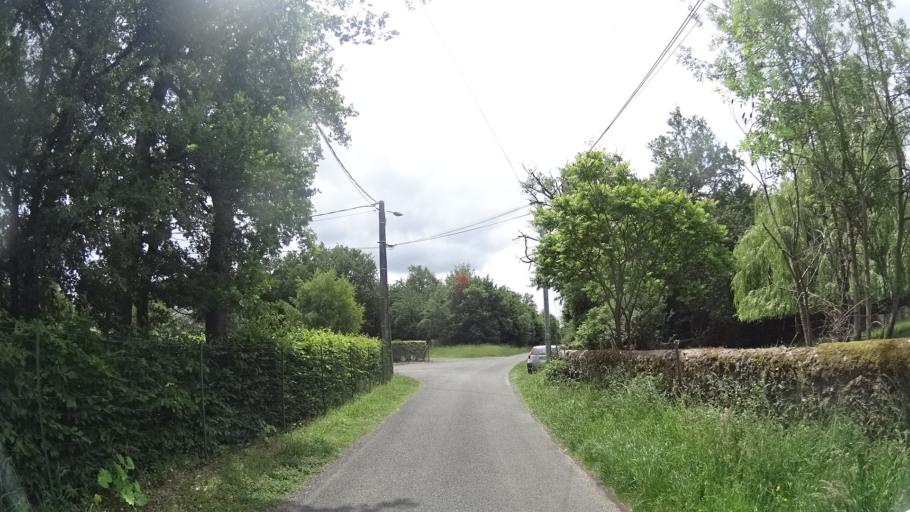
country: FR
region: Pays de la Loire
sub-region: Departement de Maine-et-Loire
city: Chenehutte-Treves-Cunault
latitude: 47.3026
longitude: -0.1529
